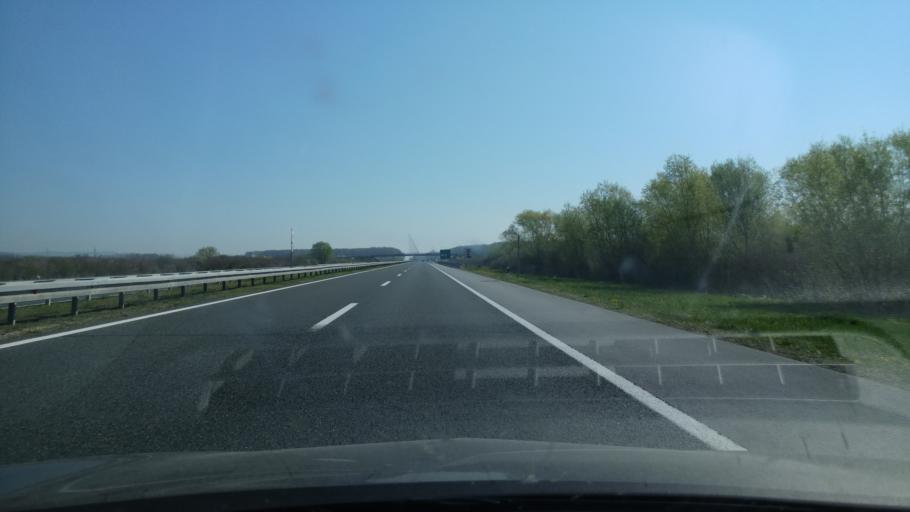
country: HR
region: Brodsko-Posavska
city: Oriovac
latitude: 45.1549
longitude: 17.8080
